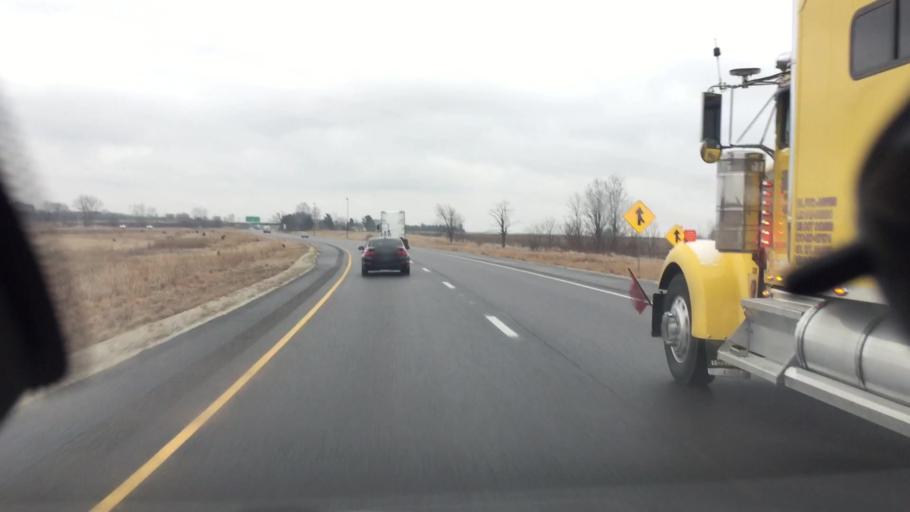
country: US
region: Illinois
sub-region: Tazewell County
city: Morton
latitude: 40.6325
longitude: -89.5182
